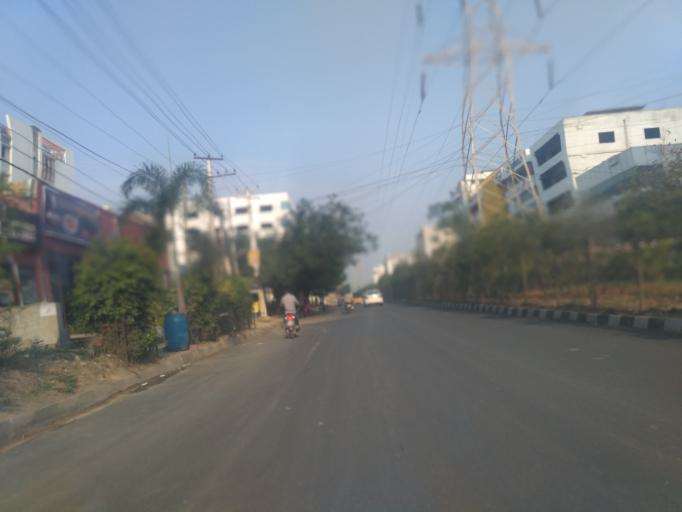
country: IN
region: Telangana
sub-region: Rangareddi
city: Kukatpalli
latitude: 17.4516
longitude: 78.3945
